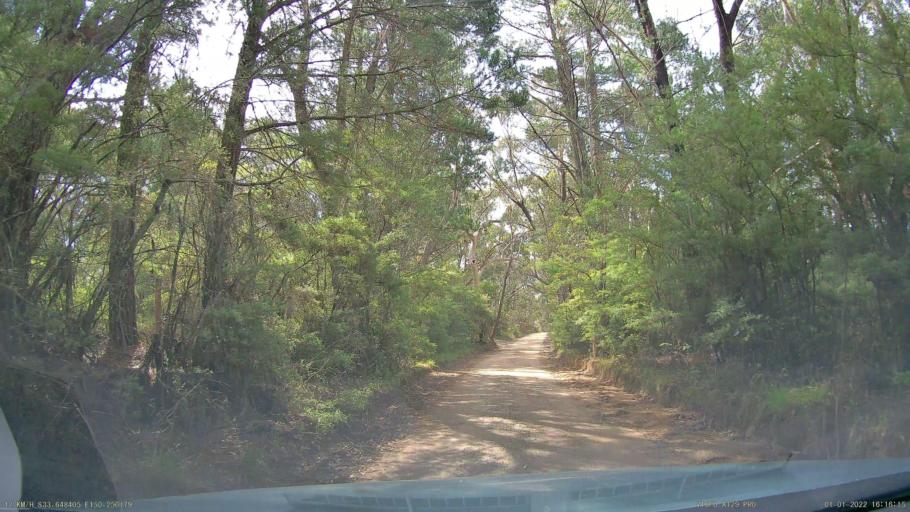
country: AU
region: New South Wales
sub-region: Blue Mountains Municipality
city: Blackheath
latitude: -33.6484
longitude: 150.2501
